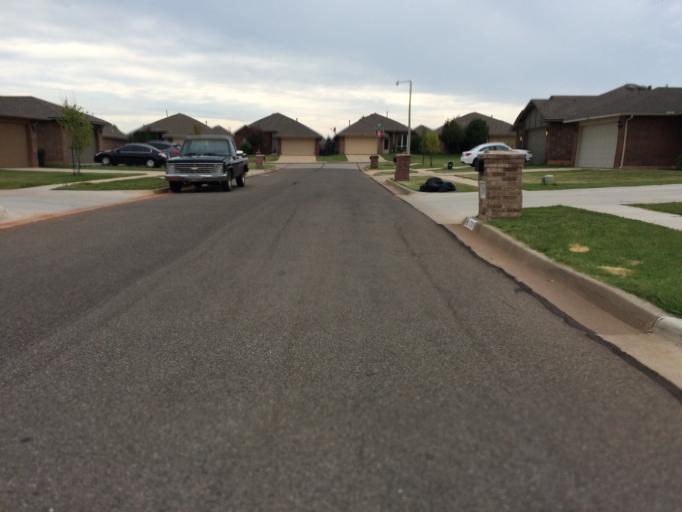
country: US
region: Oklahoma
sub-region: Cleveland County
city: Hall Park
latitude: 35.2499
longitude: -97.4182
